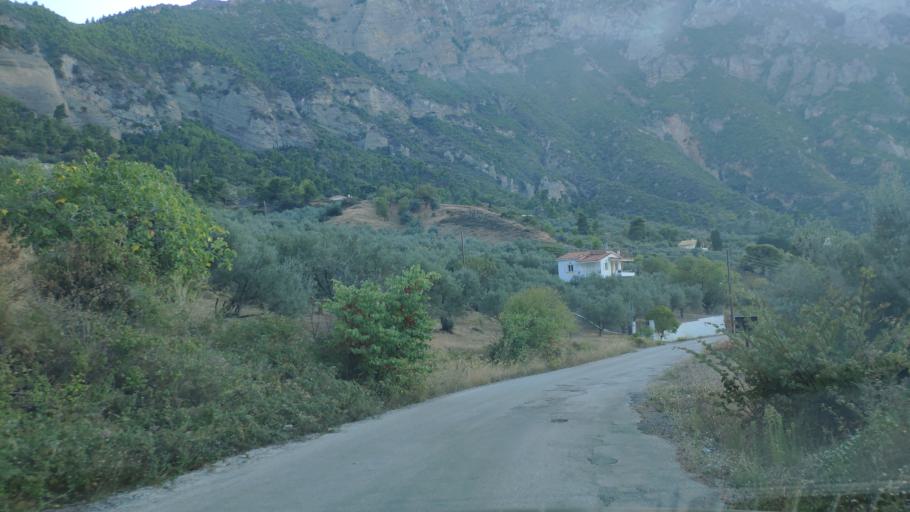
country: GR
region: West Greece
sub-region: Nomos Achaias
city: Aiyira
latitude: 38.0989
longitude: 22.4043
